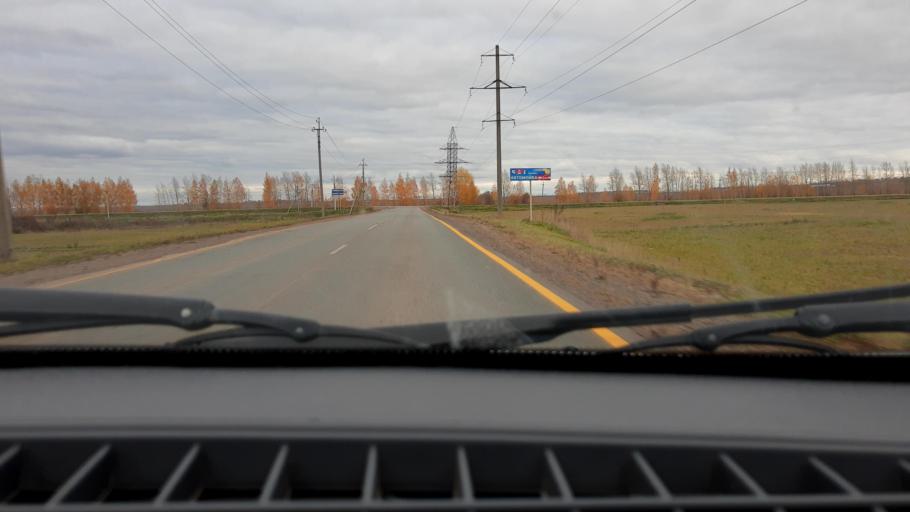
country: RU
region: Bashkortostan
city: Kabakovo
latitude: 54.5375
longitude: 56.0683
